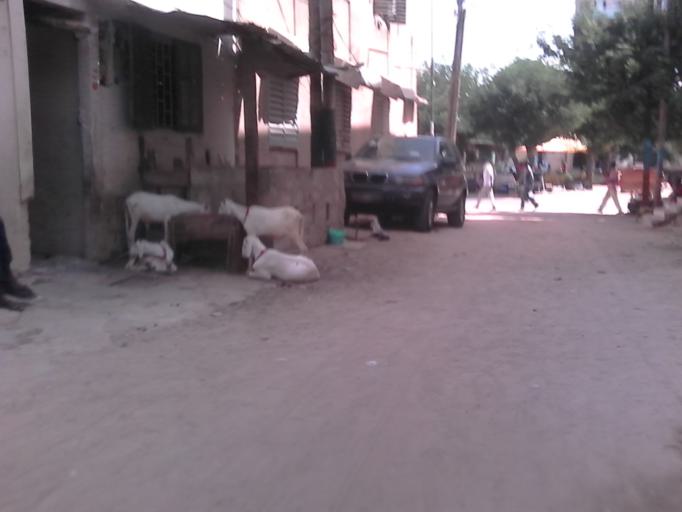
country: SN
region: Dakar
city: Grand Dakar
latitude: 14.7054
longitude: -17.4527
